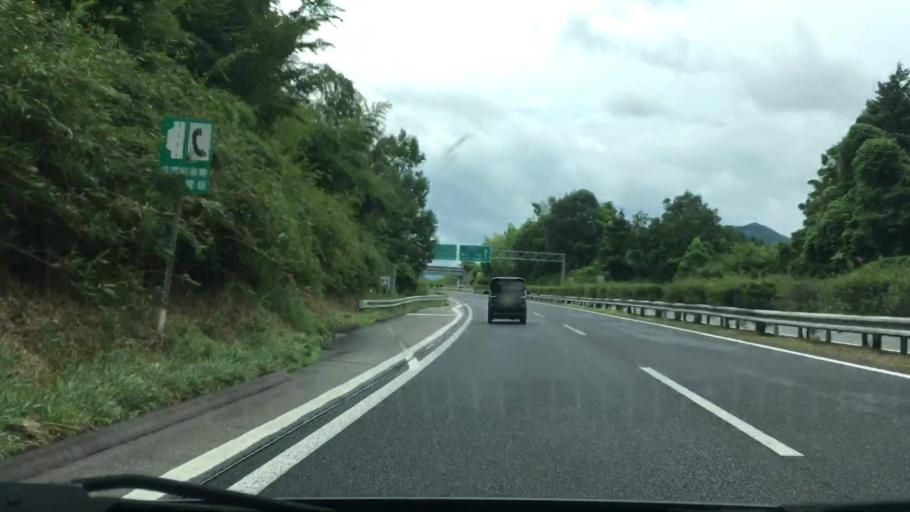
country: JP
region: Okayama
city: Tsuyama
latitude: 35.0549
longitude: 133.8131
